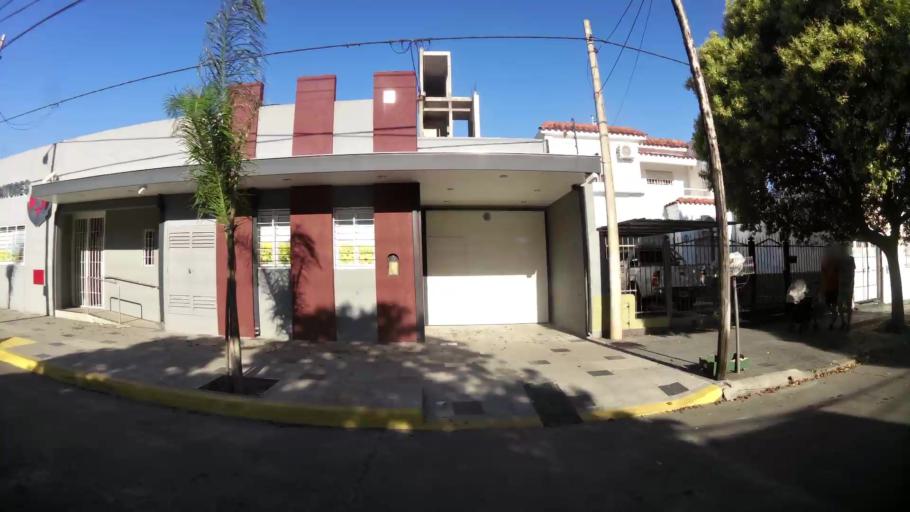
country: AR
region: Cordoba
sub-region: Departamento de Capital
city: Cordoba
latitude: -31.3880
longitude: -64.1824
